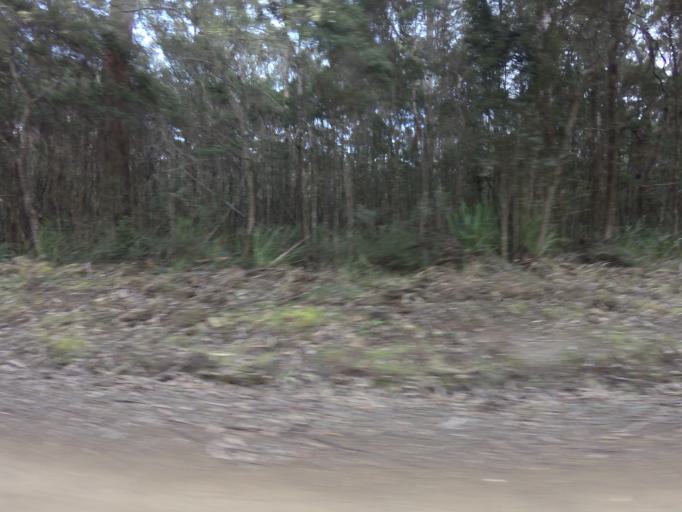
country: AU
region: Tasmania
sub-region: Huon Valley
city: Geeveston
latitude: -43.5302
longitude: 146.8953
